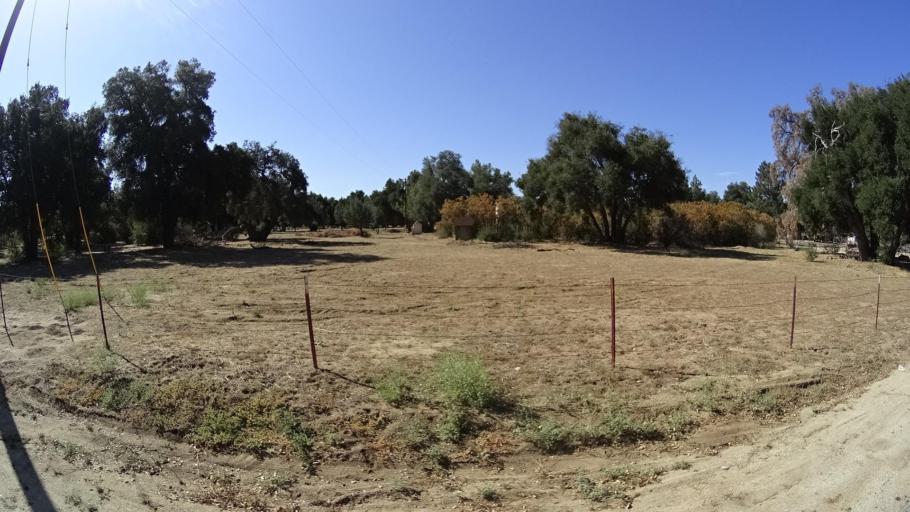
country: US
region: California
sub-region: Riverside County
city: Anza
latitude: 33.3844
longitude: -116.6831
